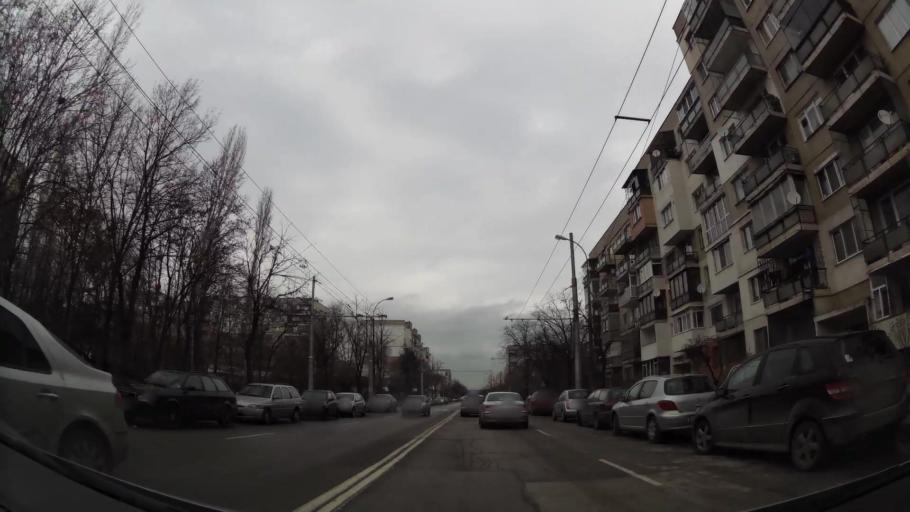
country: BG
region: Sofiya
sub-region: Obshtina Bozhurishte
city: Bozhurishte
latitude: 42.7270
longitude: 23.2524
